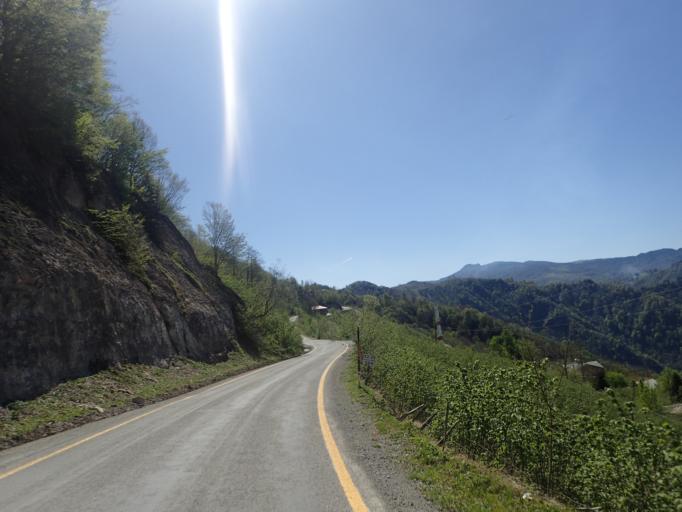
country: TR
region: Ordu
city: Kabaduz
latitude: 40.8047
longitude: 37.9056
